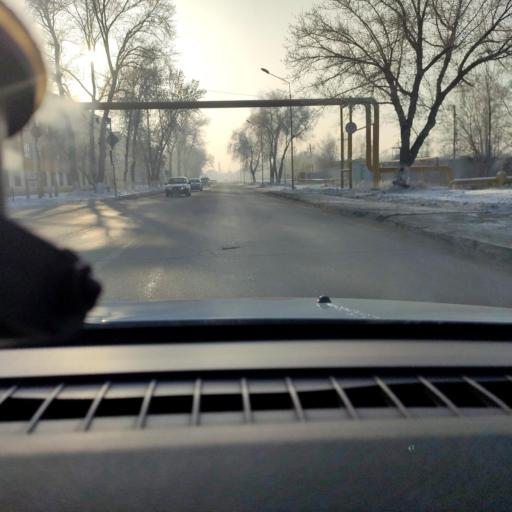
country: RU
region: Samara
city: Chapayevsk
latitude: 52.9736
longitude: 49.7016
